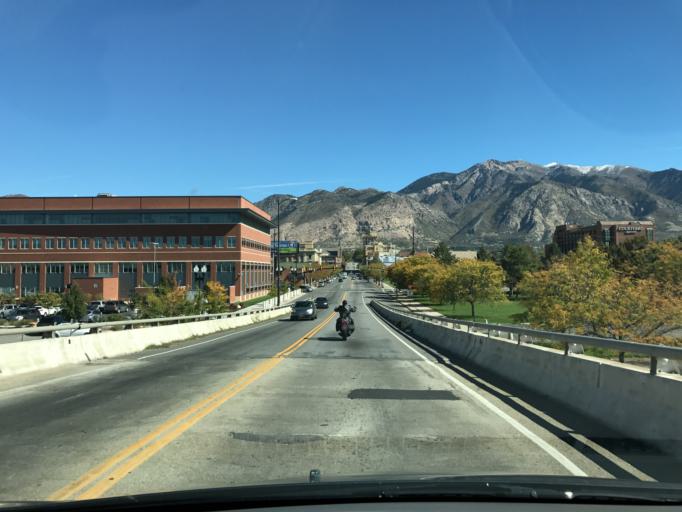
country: US
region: Utah
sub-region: Weber County
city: Ogden
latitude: 41.2228
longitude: -111.9777
